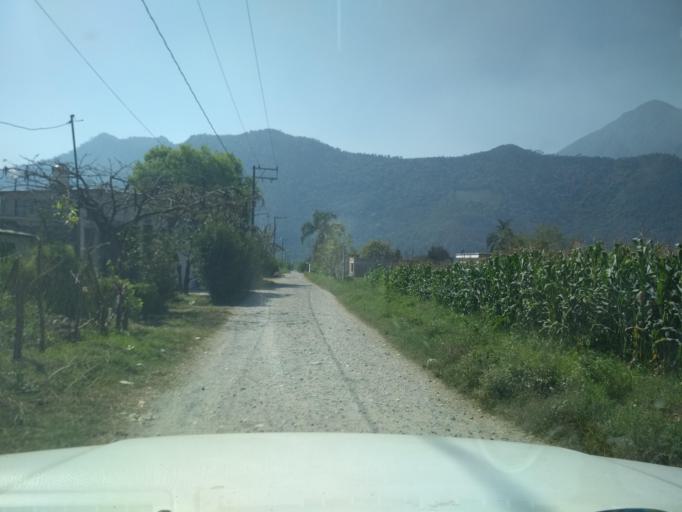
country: MX
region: Veracruz
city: Jalapilla
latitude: 18.8179
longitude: -97.0876
